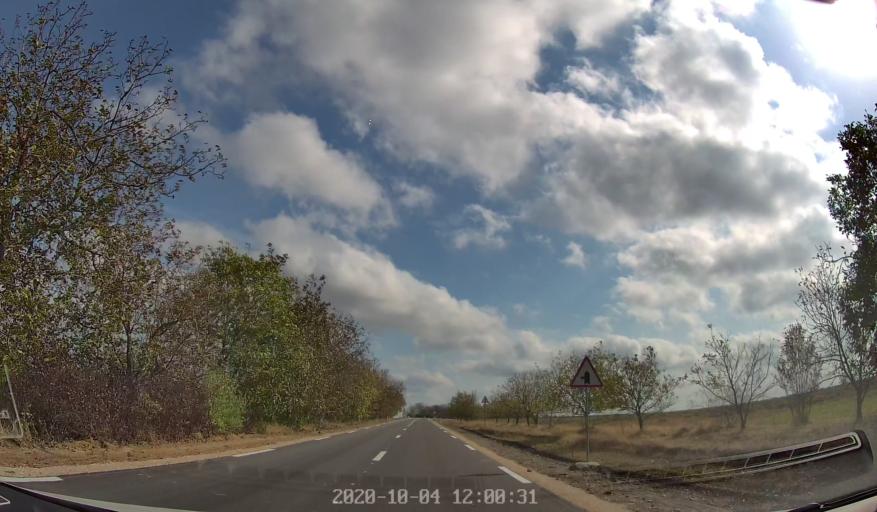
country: MD
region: Rezina
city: Saharna
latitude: 47.6308
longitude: 28.8737
